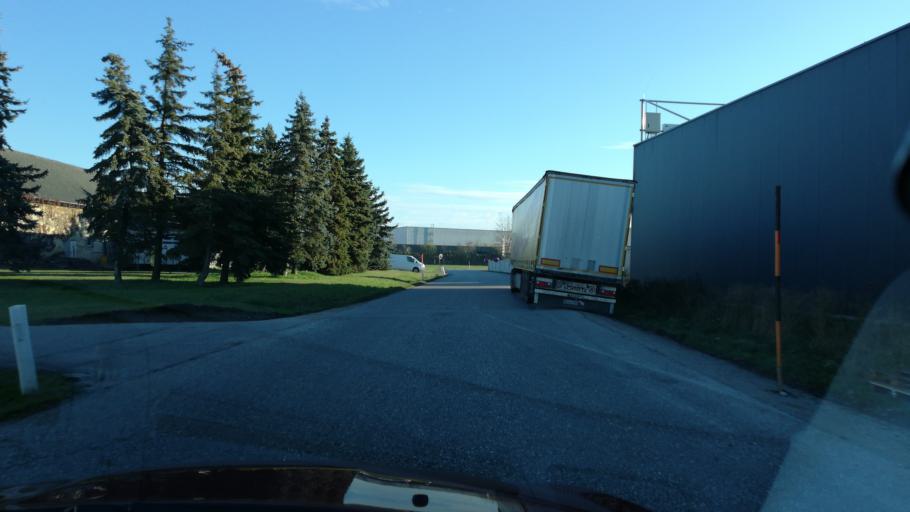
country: AT
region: Upper Austria
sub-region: Wels Stadt
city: Wels
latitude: 48.1897
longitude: 14.0590
